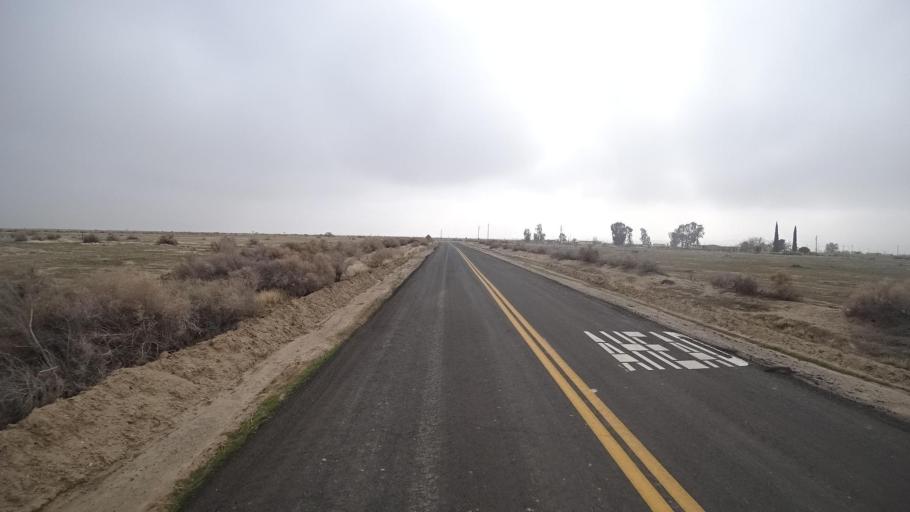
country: US
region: California
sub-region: Kern County
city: Maricopa
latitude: 35.0598
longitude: -119.3501
